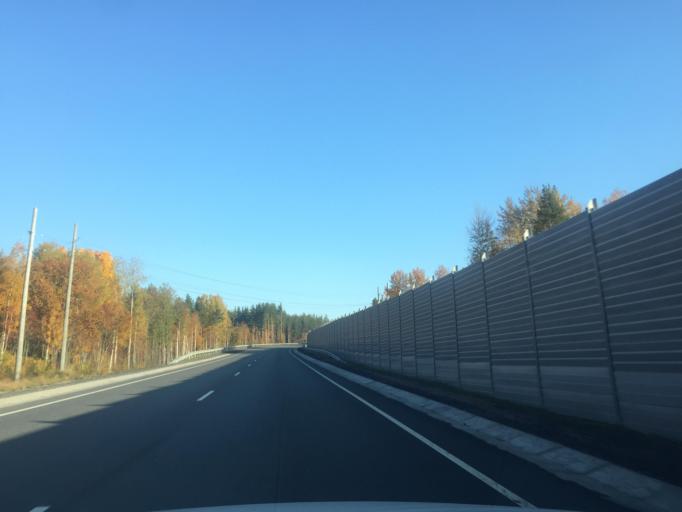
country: RU
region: Leningrad
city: Priozersk
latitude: 60.8368
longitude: 30.1227
